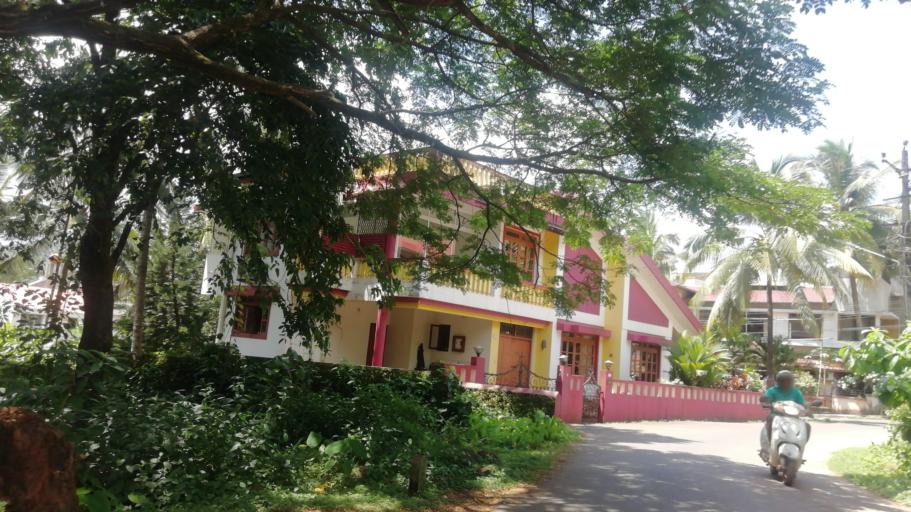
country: IN
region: Goa
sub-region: North Goa
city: Queula
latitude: 15.3943
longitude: 73.9982
